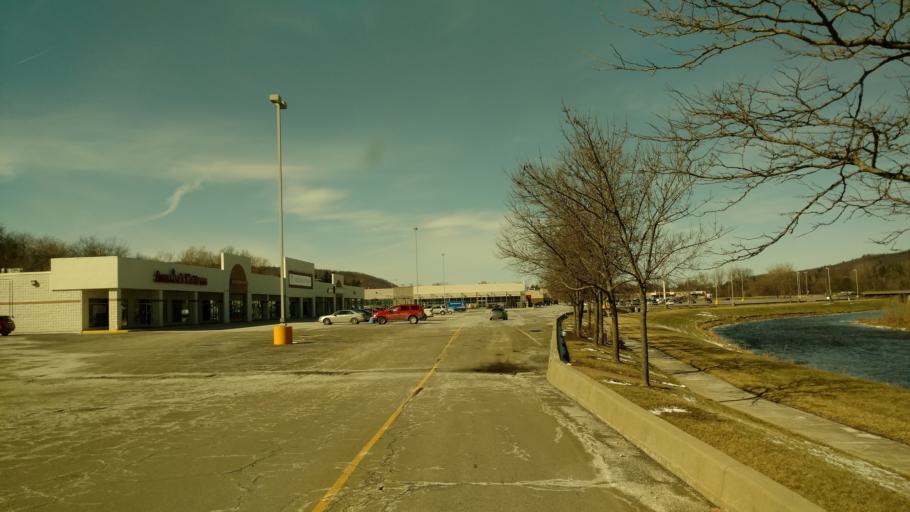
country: US
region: New York
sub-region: Allegany County
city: Wellsville
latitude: 42.1242
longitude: -77.9607
